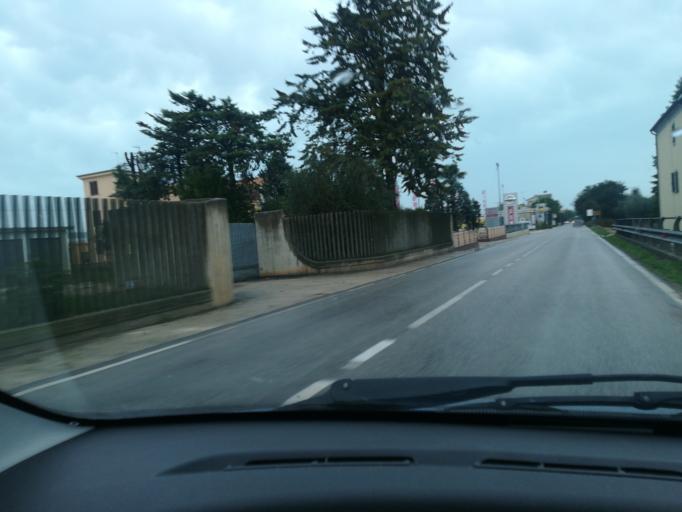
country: IT
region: The Marches
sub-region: Provincia di Macerata
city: Borgo Stazione
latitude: 43.2808
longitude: 13.6284
